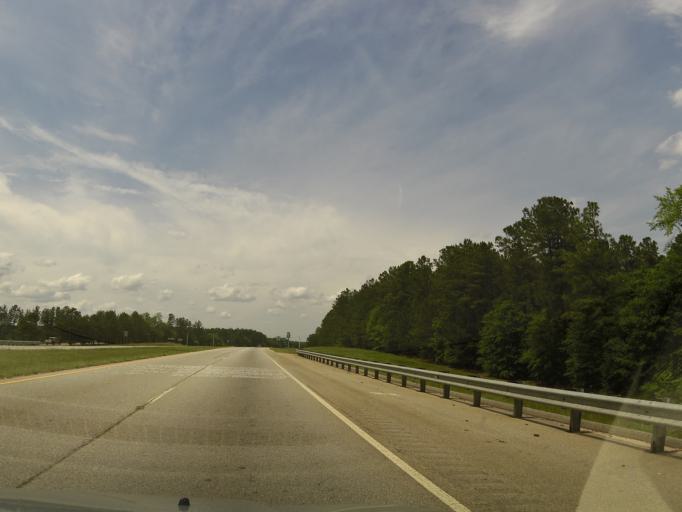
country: US
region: Georgia
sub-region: Emanuel County
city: Swainsboro
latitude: 32.5741
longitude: -82.3567
